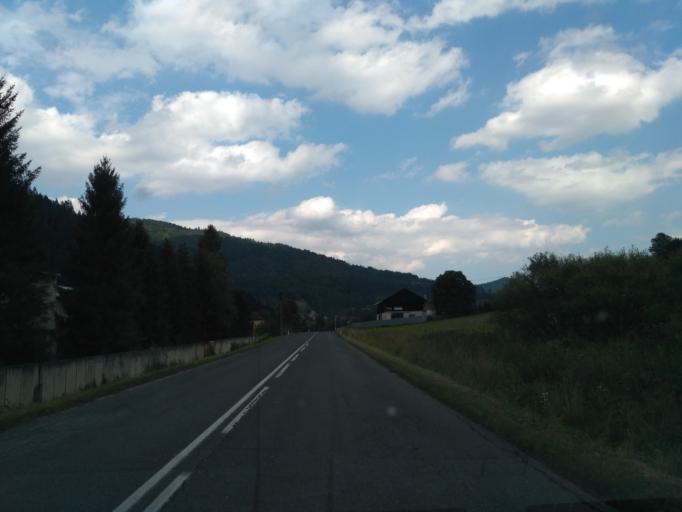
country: SK
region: Kosicky
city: Gelnica
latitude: 48.8623
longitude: 20.9554
